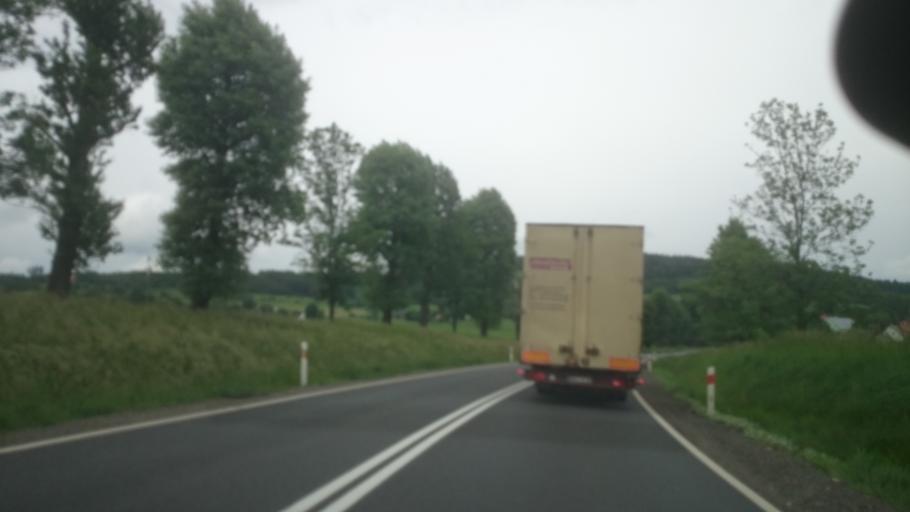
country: PL
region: Lower Silesian Voivodeship
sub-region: Powiat klodzki
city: Klodzko
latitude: 50.4369
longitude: 16.6915
